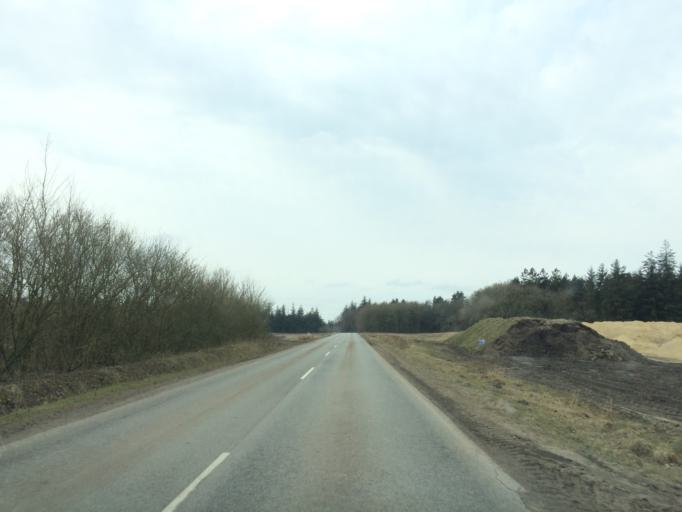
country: DK
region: Central Jutland
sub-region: Ringkobing-Skjern Kommune
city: Tarm
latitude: 55.8475
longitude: 8.4847
